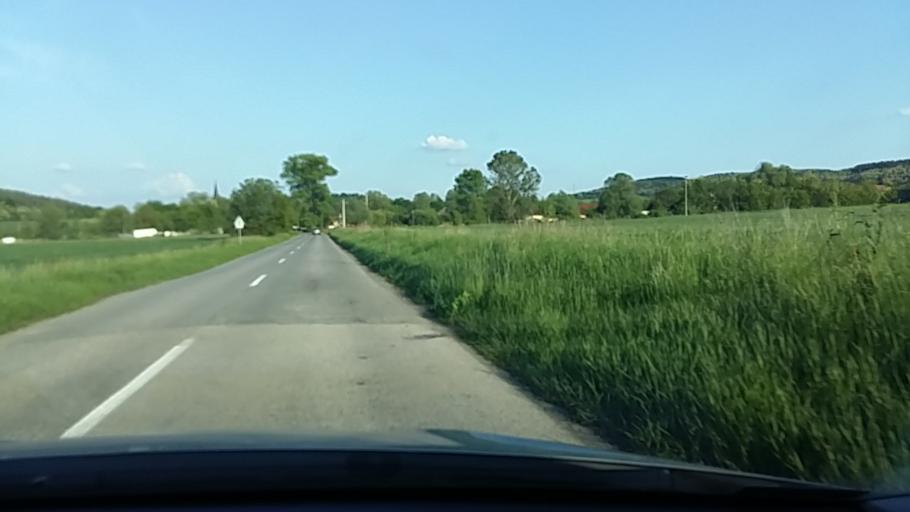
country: HU
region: Pest
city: Szod
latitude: 47.7517
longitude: 19.2042
